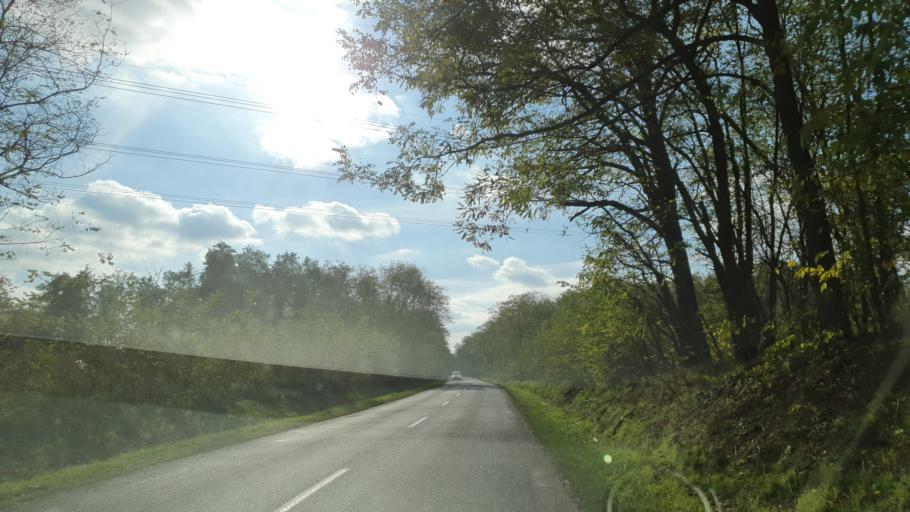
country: HU
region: Szabolcs-Szatmar-Bereg
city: Anarcs
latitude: 48.1563
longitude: 22.0940
